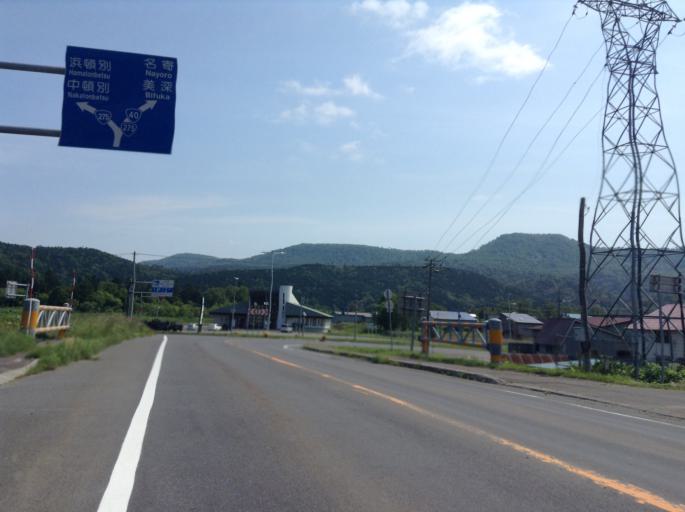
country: JP
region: Hokkaido
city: Nayoro
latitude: 44.7281
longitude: 142.2561
